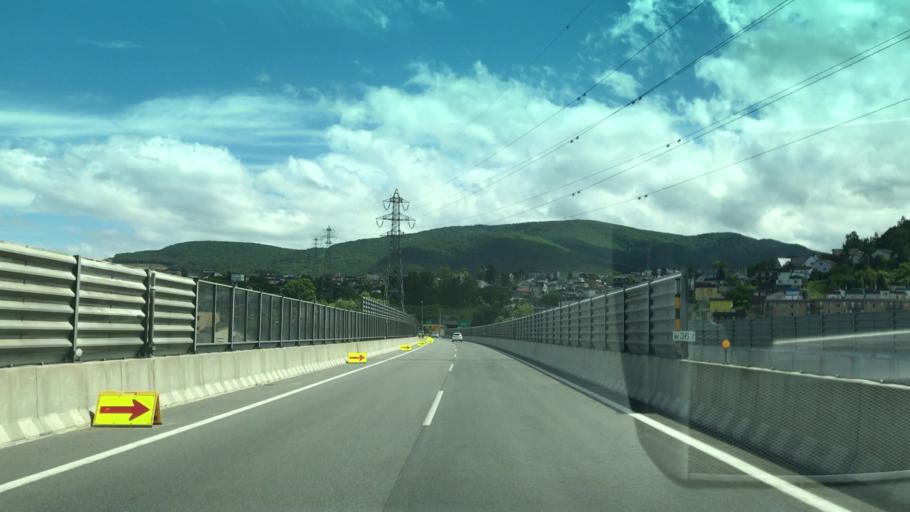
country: JP
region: Hokkaido
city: Otaru
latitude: 43.1721
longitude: 141.0334
